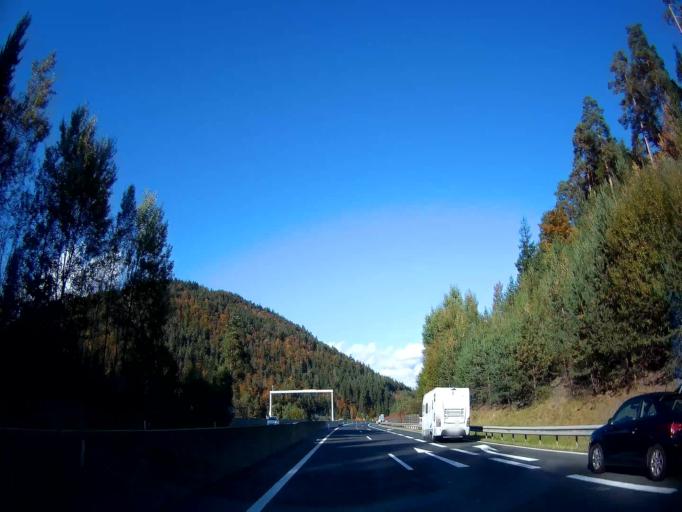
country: AT
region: Carinthia
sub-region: Politischer Bezirk Volkermarkt
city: Voelkermarkt
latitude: 46.6506
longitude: 14.5619
